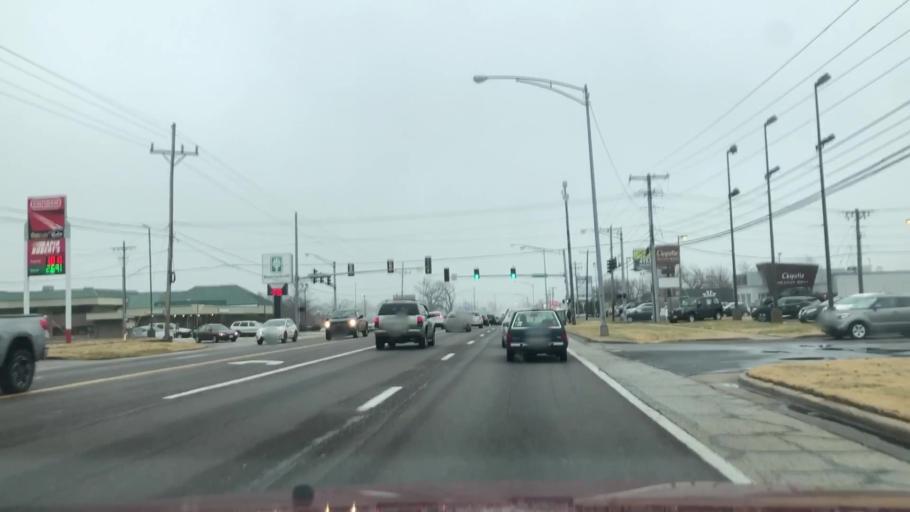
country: US
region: Missouri
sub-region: Greene County
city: Springfield
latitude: 37.1519
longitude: -93.2958
